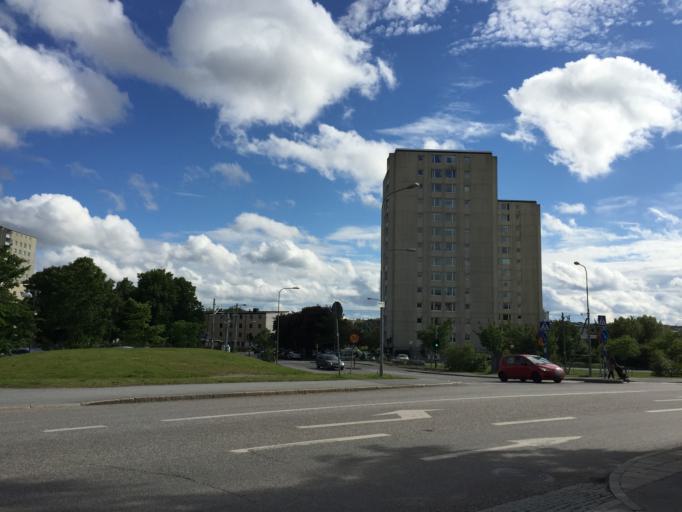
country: SE
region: Stockholm
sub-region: Stockholms Kommun
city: Arsta
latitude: 59.2968
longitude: 18.0433
